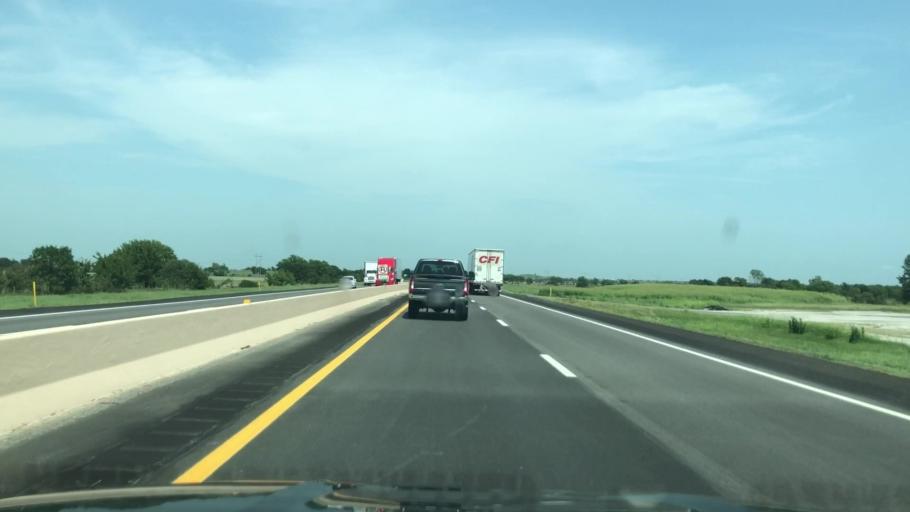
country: US
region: Oklahoma
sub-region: Craig County
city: Vinita
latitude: 36.6699
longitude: -95.0687
